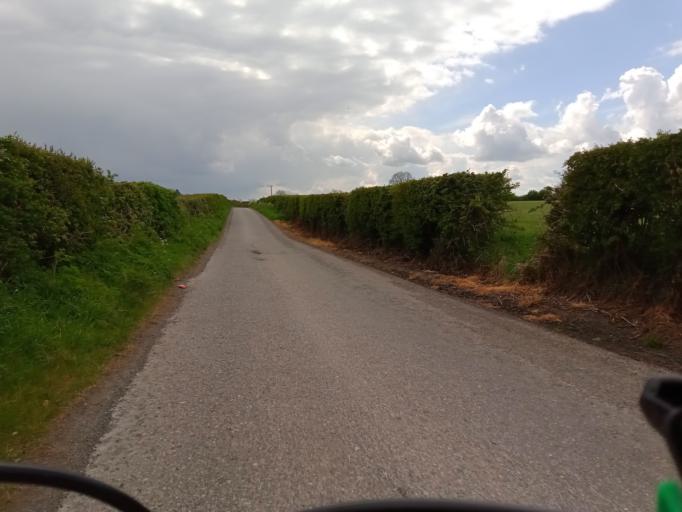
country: IE
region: Leinster
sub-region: Kilkenny
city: Kilkenny
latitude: 52.6261
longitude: -7.2911
